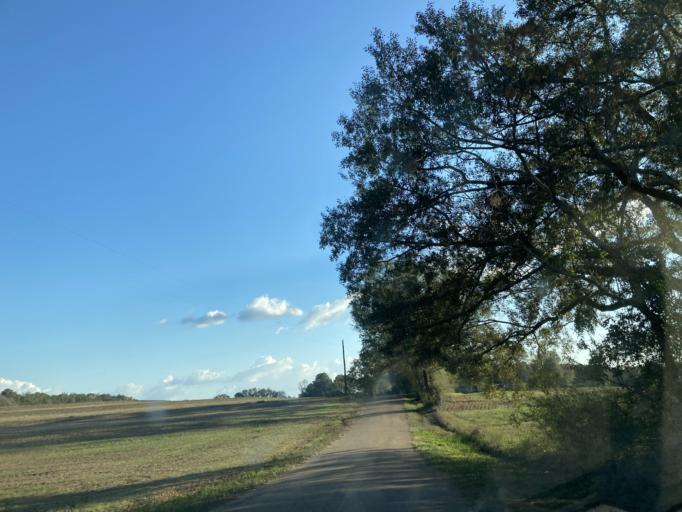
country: US
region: Mississippi
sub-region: Lamar County
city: Sumrall
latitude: 31.4010
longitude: -89.6201
